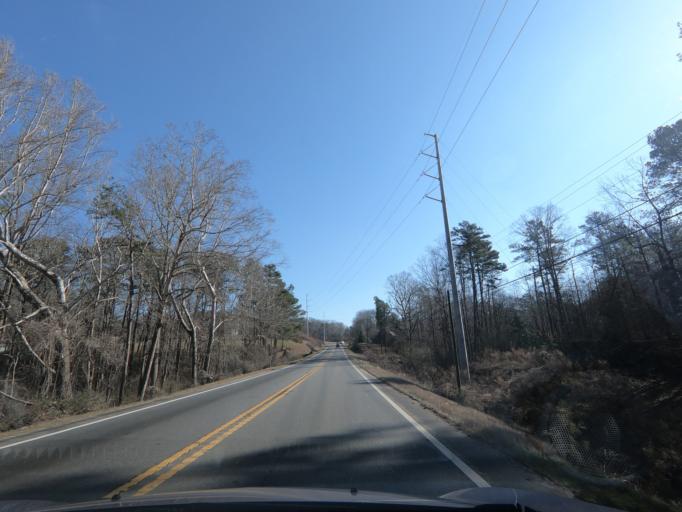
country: US
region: Georgia
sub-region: Forsyth County
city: Cumming
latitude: 34.3020
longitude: -84.1946
